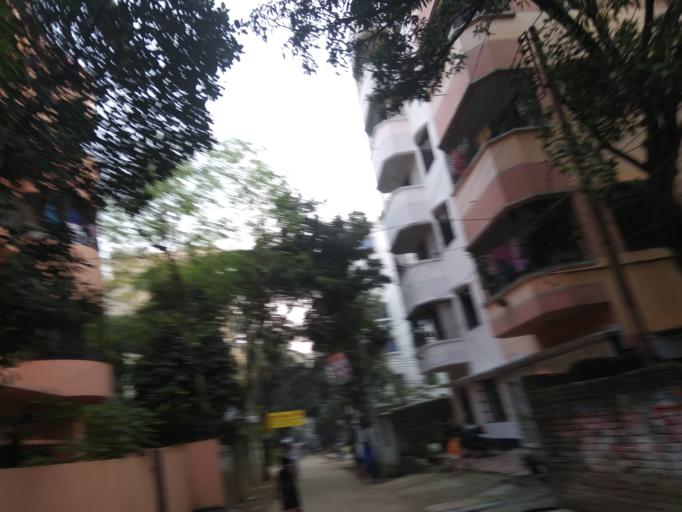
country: BD
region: Dhaka
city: Tungi
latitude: 23.8149
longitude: 90.3641
